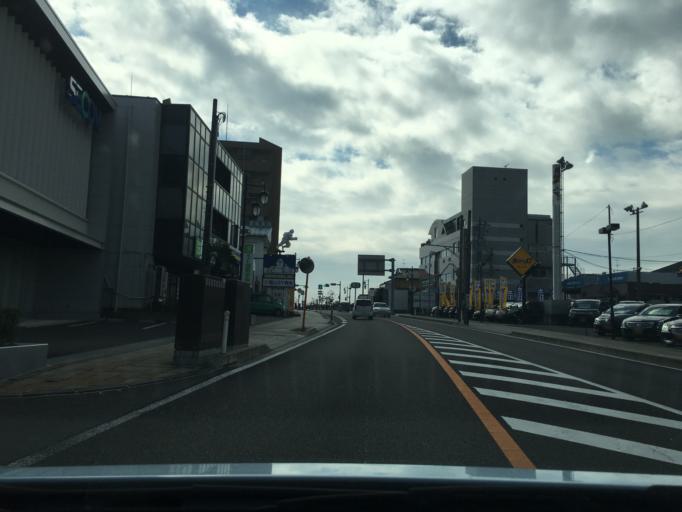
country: JP
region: Fukushima
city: Koriyama
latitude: 37.3914
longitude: 140.3551
